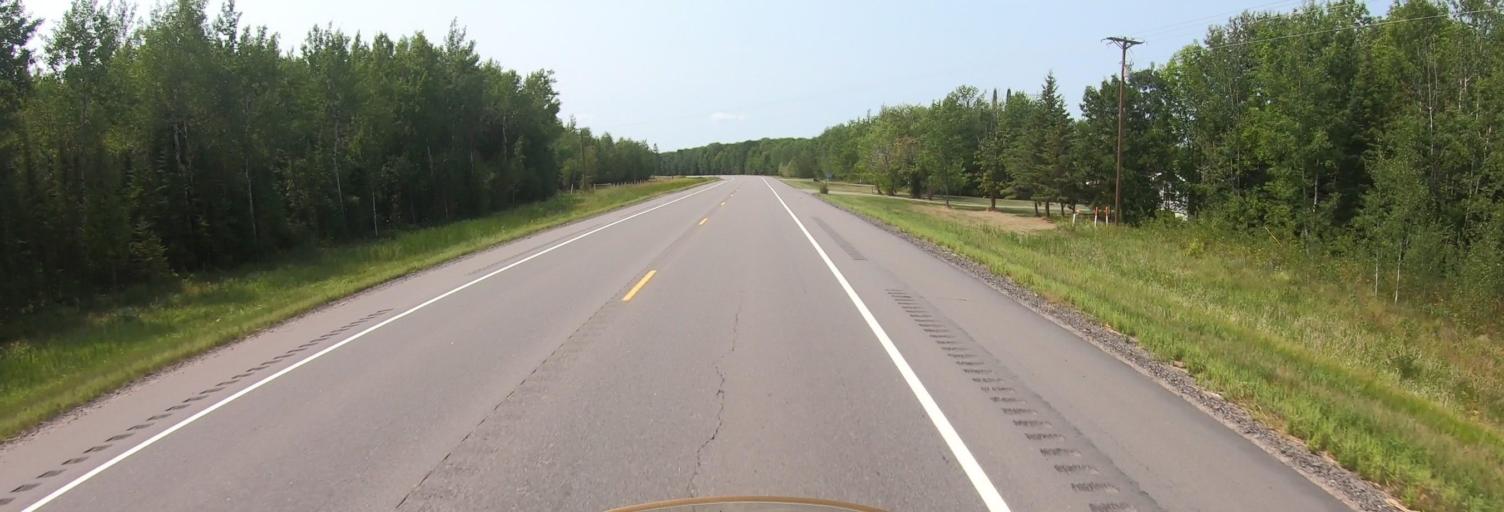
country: US
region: Minnesota
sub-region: Koochiching County
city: International Falls
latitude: 48.5304
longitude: -93.5208
